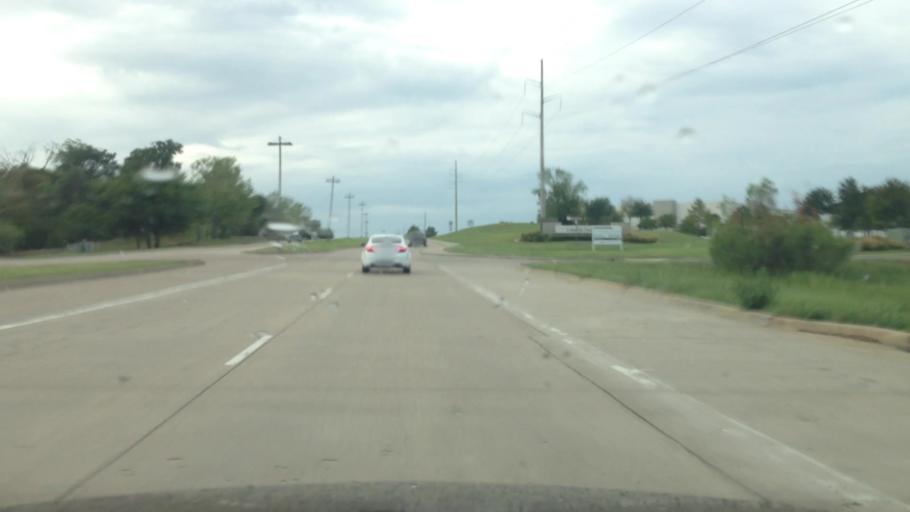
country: US
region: Texas
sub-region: Dallas County
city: Coppell
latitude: 32.9877
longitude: -97.0304
